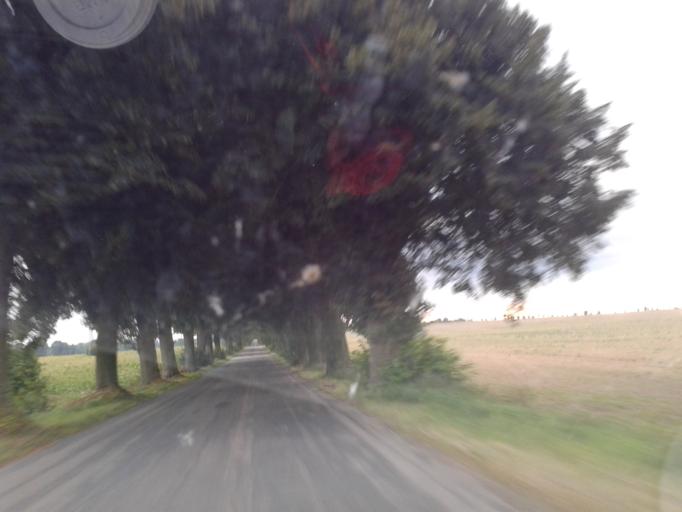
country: PL
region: West Pomeranian Voivodeship
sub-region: Powiat szczecinecki
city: Grzmiaca
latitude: 53.8468
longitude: 16.4532
